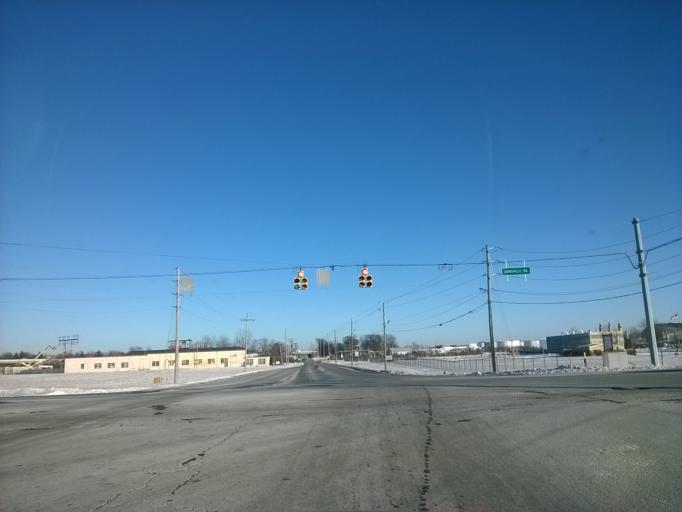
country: US
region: Indiana
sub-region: Boone County
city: Zionsville
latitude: 39.9251
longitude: -86.2601
